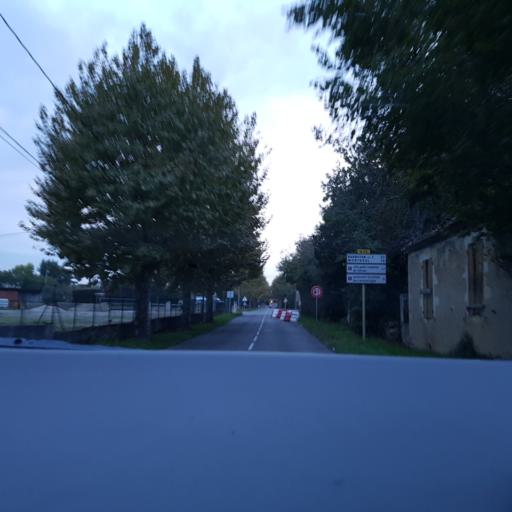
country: FR
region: Midi-Pyrenees
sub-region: Departement du Gers
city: Condom
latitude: 43.9539
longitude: 0.3621
